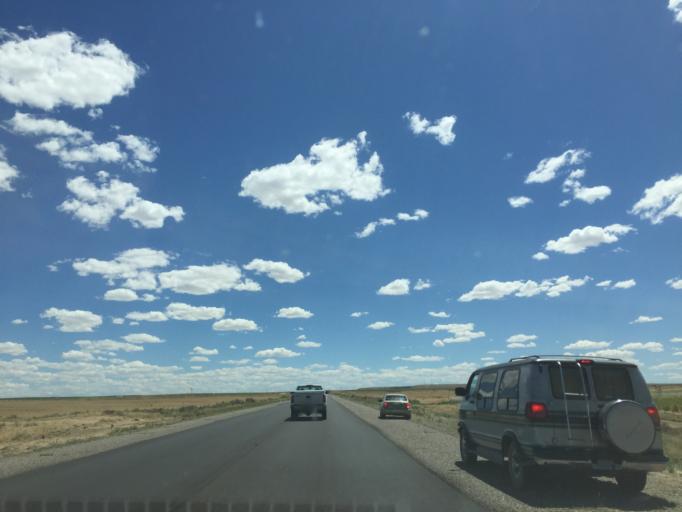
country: US
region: New Mexico
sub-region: San Juan County
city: Farmington
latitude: 36.5364
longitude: -108.2340
